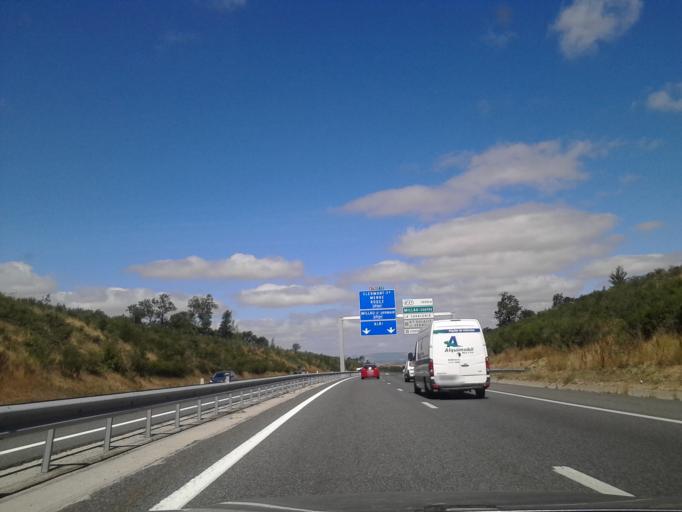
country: FR
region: Midi-Pyrenees
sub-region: Departement de l'Aveyron
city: La Cavalerie
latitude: 44.0006
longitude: 3.1569
